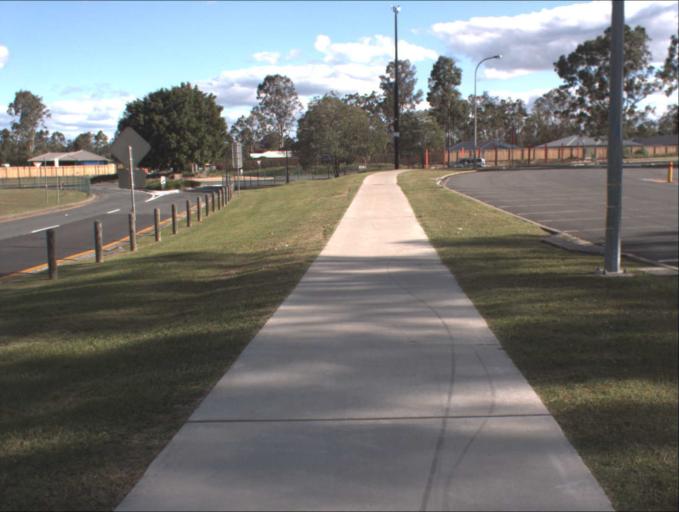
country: AU
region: Queensland
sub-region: Logan
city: North Maclean
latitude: -27.8083
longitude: 152.9559
